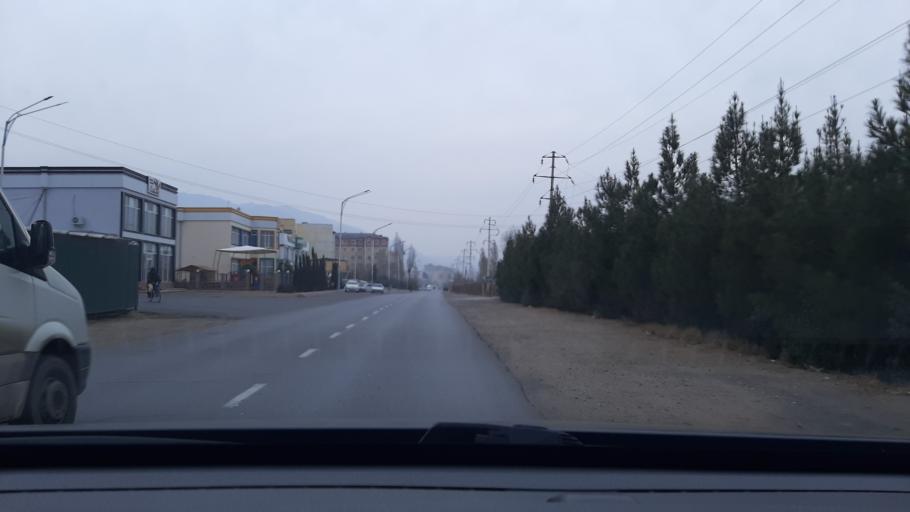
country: TJ
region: Viloyati Sughd
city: Khujand
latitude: 40.2789
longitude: 69.5831
